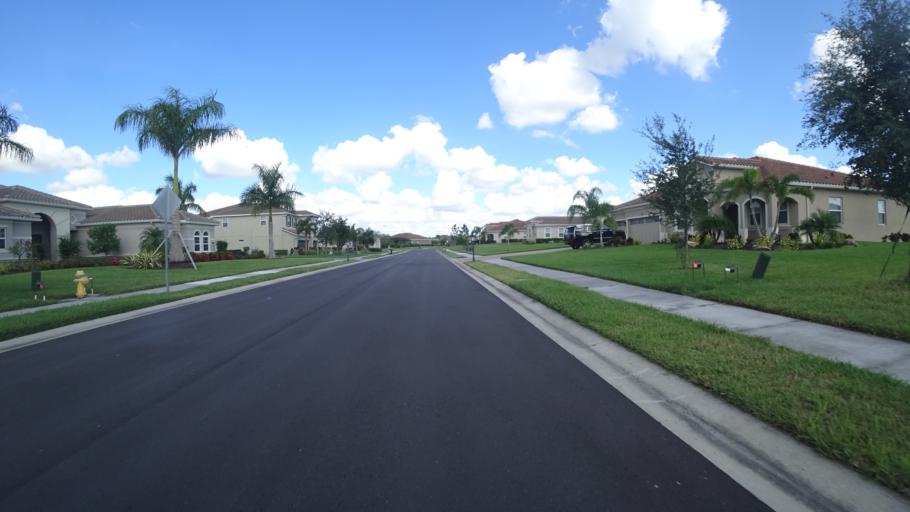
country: US
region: Florida
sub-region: Manatee County
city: Ellenton
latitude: 27.4968
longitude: -82.3707
